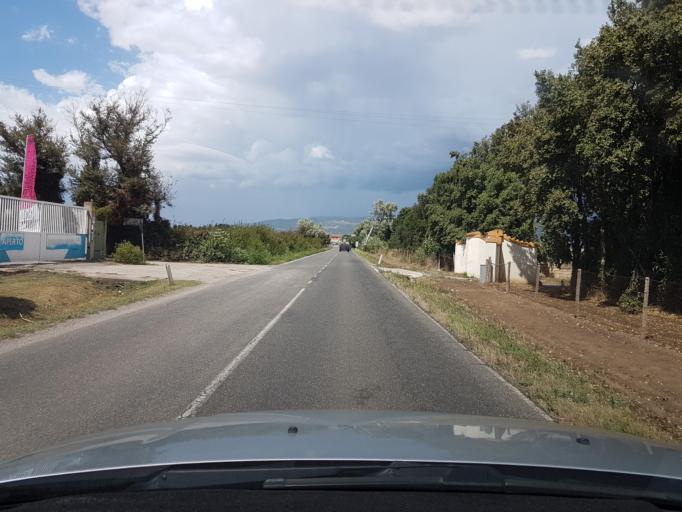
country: IT
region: Sardinia
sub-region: Provincia di Oristano
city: Riola Sardo
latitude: 39.9854
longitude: 8.5401
